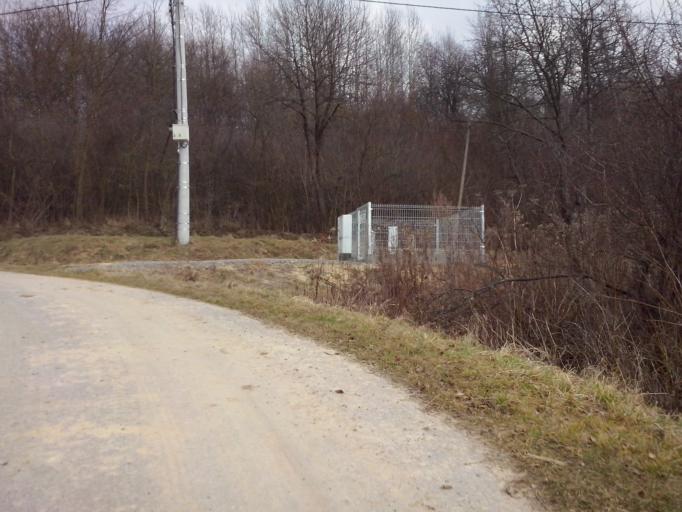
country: PL
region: Subcarpathian Voivodeship
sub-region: Powiat nizanski
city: Krzeszow
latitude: 50.4162
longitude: 22.3271
